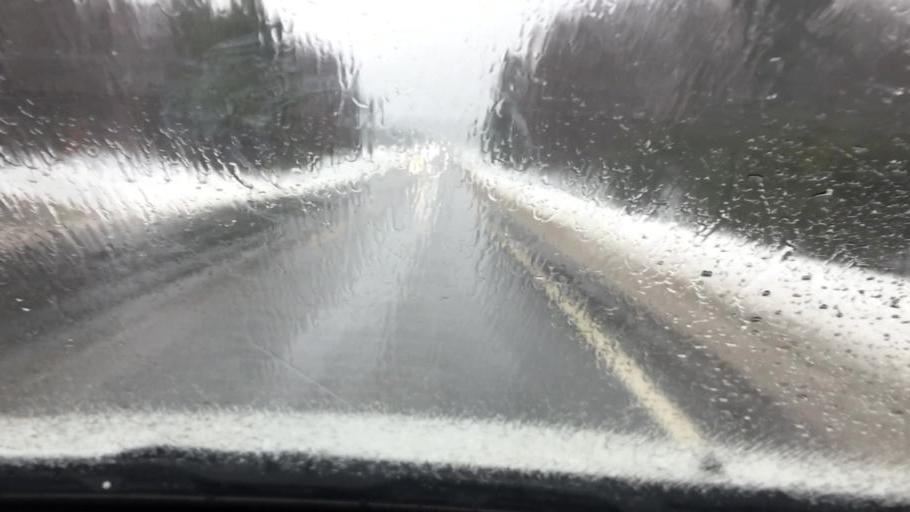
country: US
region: Michigan
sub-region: Antrim County
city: Mancelona
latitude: 44.9660
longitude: -85.0532
